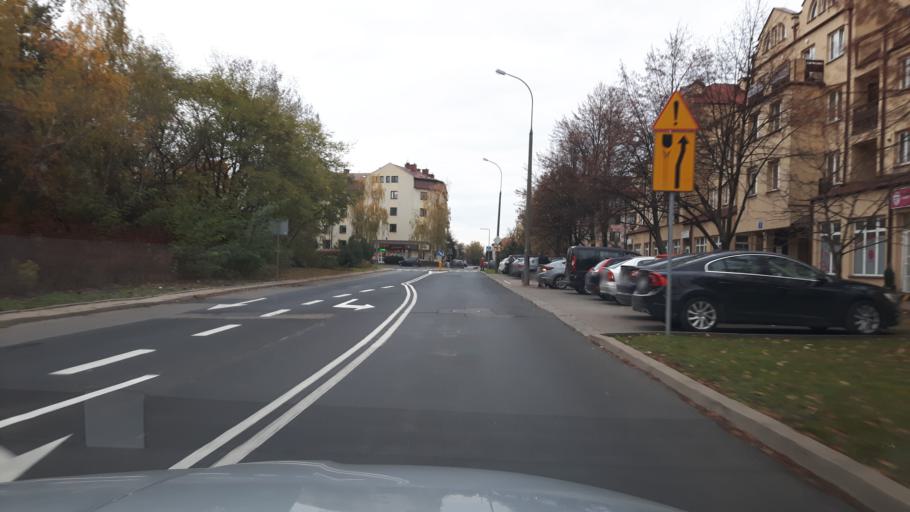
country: PL
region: Masovian Voivodeship
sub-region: Warszawa
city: Ursynow
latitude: 52.1561
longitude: 21.0549
